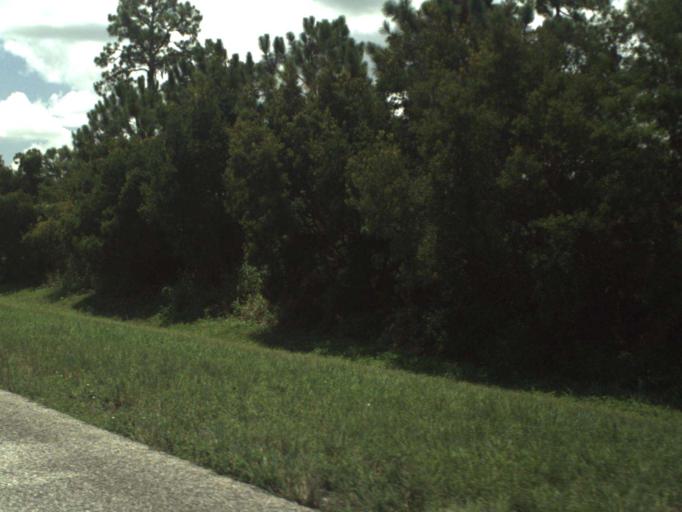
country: US
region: Florida
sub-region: Indian River County
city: Fellsmere
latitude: 27.6757
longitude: -80.8128
